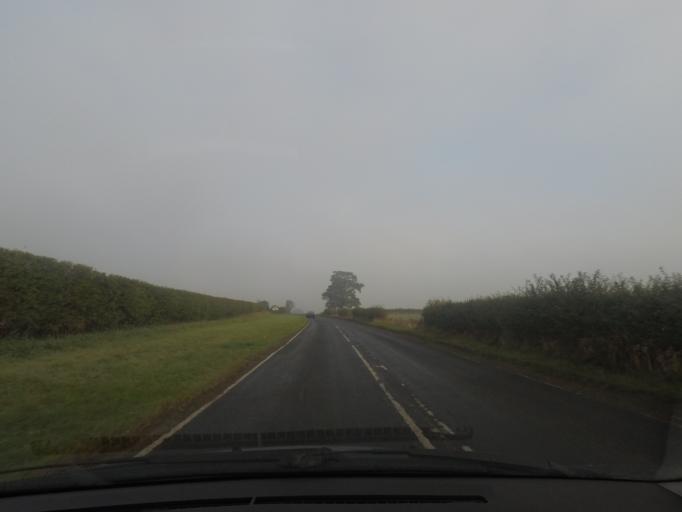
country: GB
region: England
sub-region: City and Borough of Leeds
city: Walton
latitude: 54.0207
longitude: -1.3136
